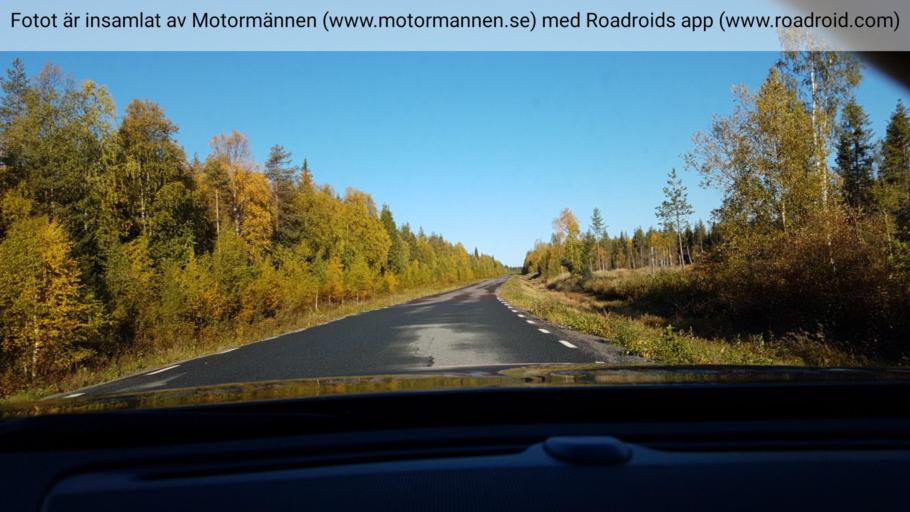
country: SE
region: Norrbotten
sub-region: Bodens Kommun
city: Boden
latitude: 66.0235
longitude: 21.4947
